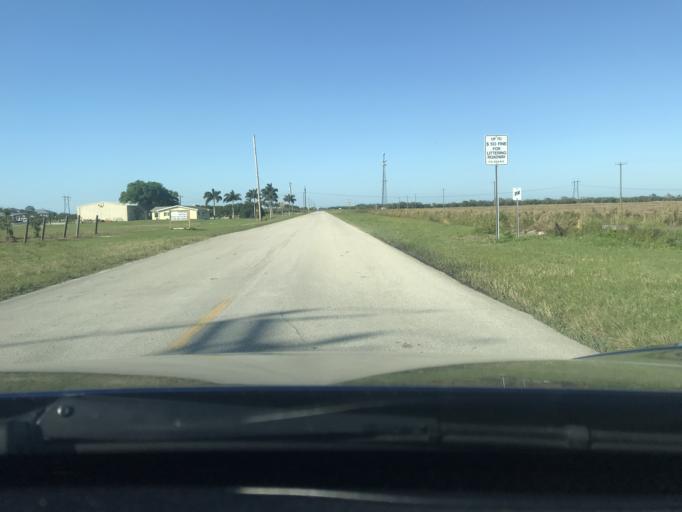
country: US
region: Florida
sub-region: Saint Lucie County
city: Fort Pierce South
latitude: 27.3745
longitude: -80.4977
